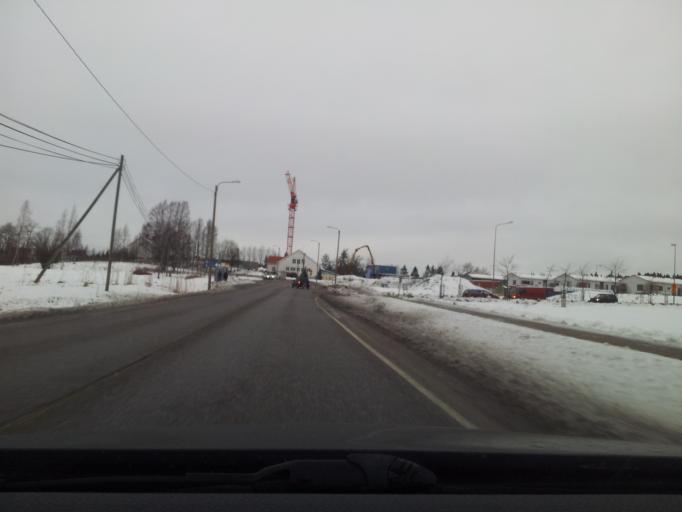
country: FI
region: Uusimaa
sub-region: Helsinki
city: Kirkkonummi
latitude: 60.1523
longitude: 24.5465
